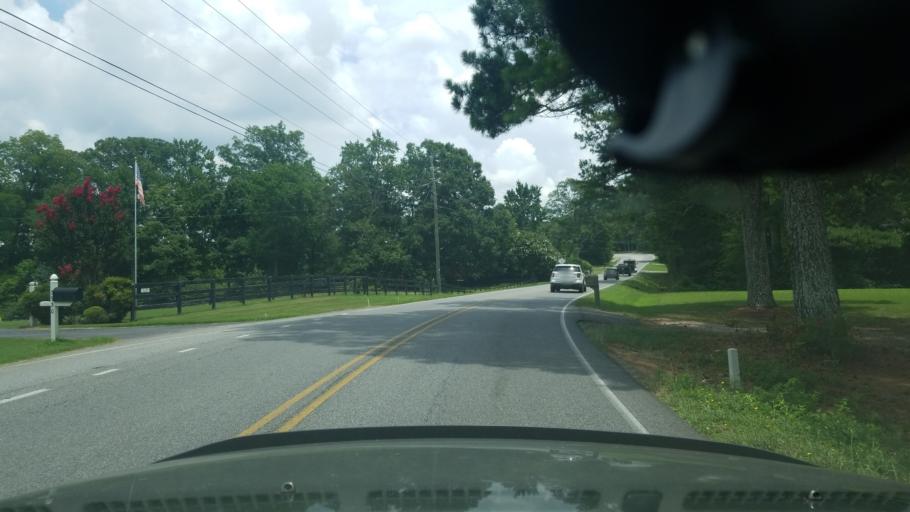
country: US
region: Georgia
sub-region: Forsyth County
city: Cumming
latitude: 34.1675
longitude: -84.1991
